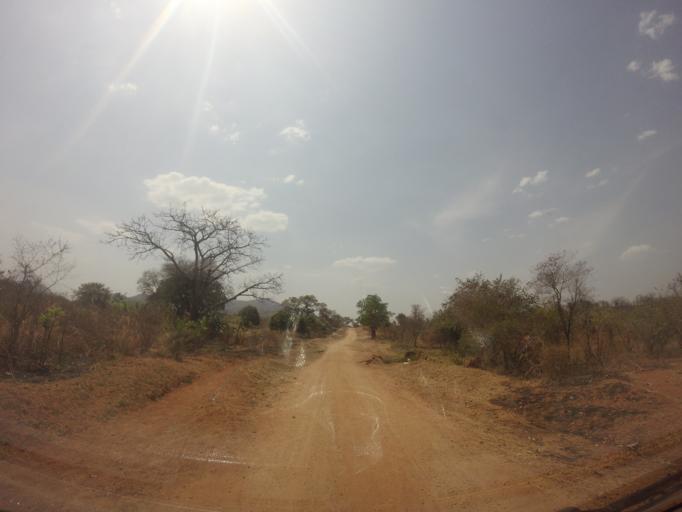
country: UG
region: Northern Region
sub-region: Arua District
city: Arua
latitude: 2.8968
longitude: 31.1174
